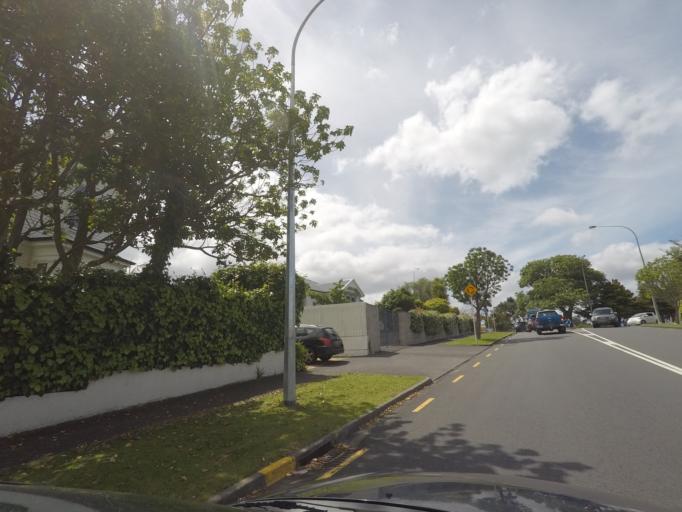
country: NZ
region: Auckland
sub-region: Auckland
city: Auckland
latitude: -36.8489
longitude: 174.7301
